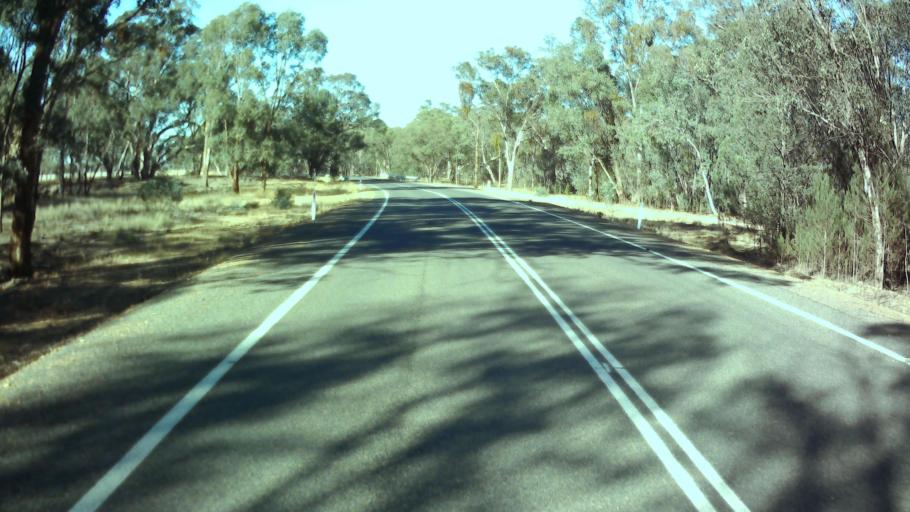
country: AU
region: New South Wales
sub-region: Weddin
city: Grenfell
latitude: -34.0023
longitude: 148.1271
